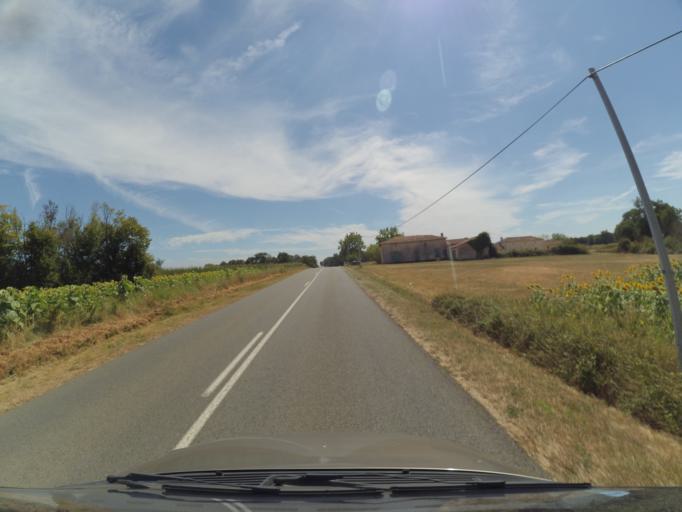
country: FR
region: Poitou-Charentes
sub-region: Departement de la Vienne
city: Usson-du-Poitou
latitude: 46.1989
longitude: 0.5358
